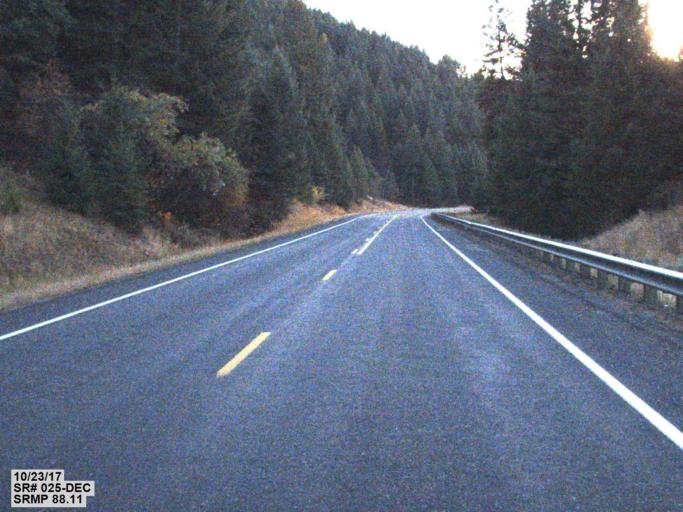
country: US
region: Washington
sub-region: Stevens County
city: Kettle Falls
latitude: 48.6742
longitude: -118.0240
